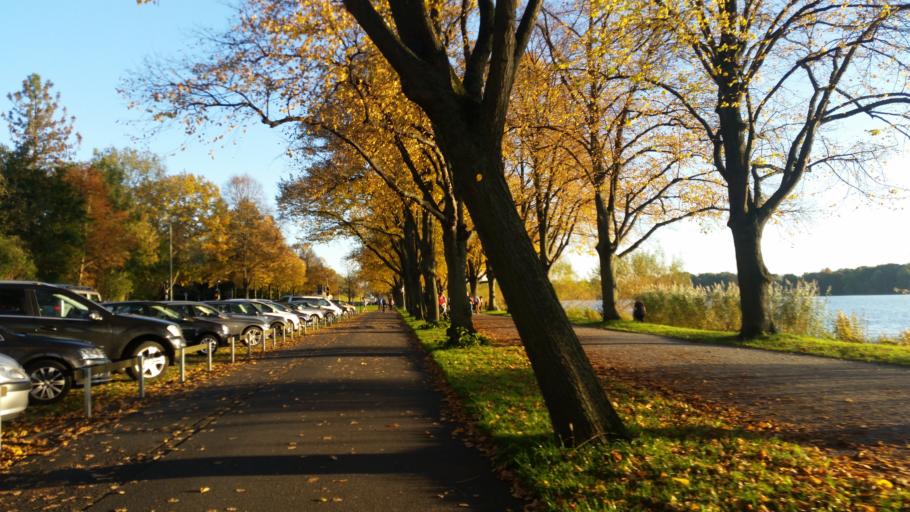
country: DE
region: Lower Saxony
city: Hannover
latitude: 52.3505
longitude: 9.7490
